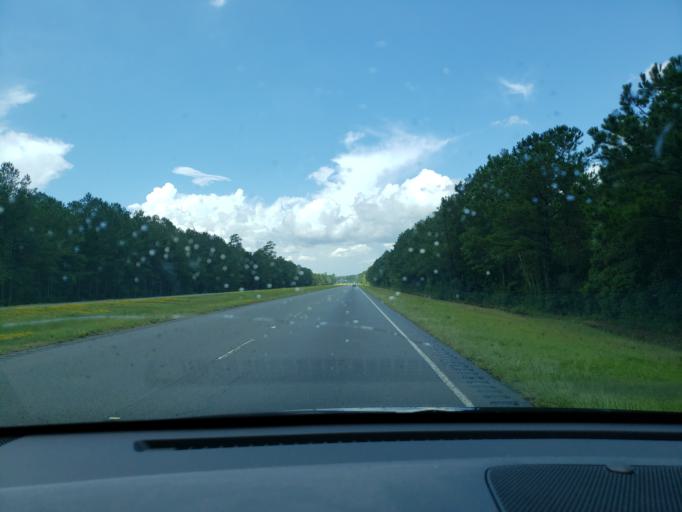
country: US
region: North Carolina
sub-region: Bladen County
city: Elizabethtown
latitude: 34.6369
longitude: -78.6642
